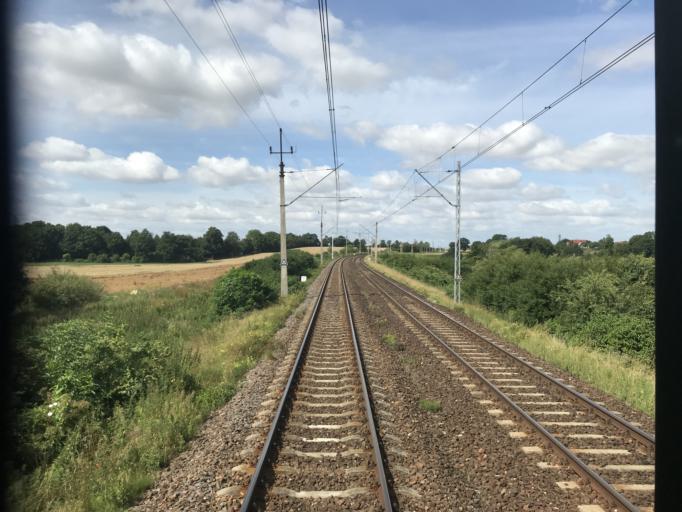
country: PL
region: Pomeranian Voivodeship
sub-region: Powiat malborski
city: Malbork
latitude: 54.0340
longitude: 19.0940
